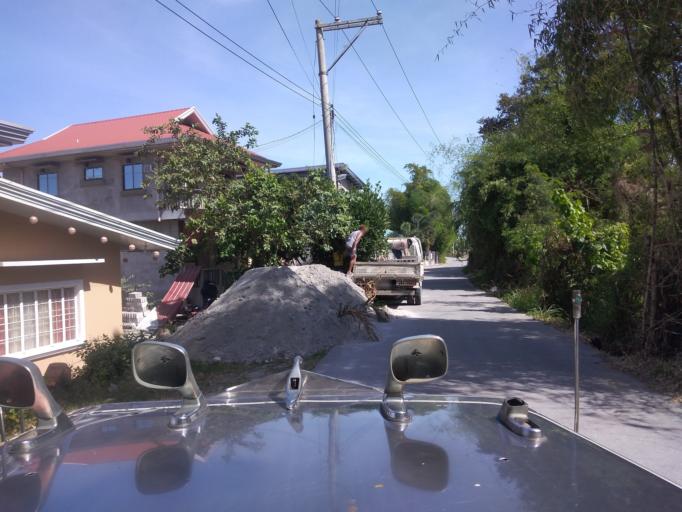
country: PH
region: Central Luzon
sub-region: Province of Pampanga
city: Magliman
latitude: 15.0269
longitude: 120.6519
